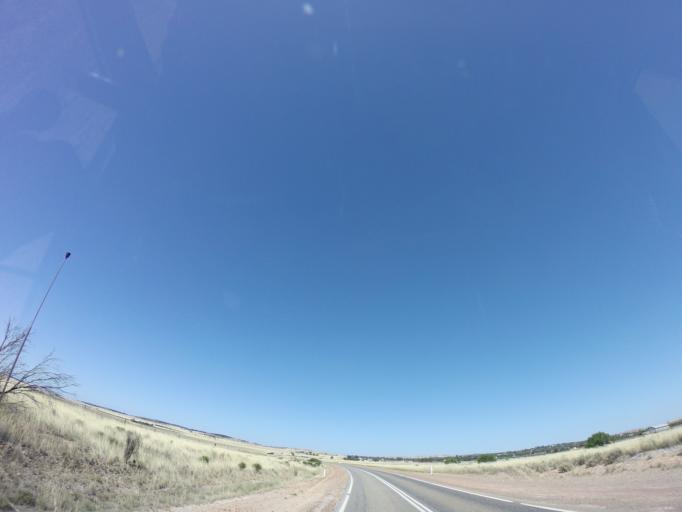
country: AU
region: South Australia
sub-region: Peterborough
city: Peterborough
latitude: -32.9688
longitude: 138.8089
